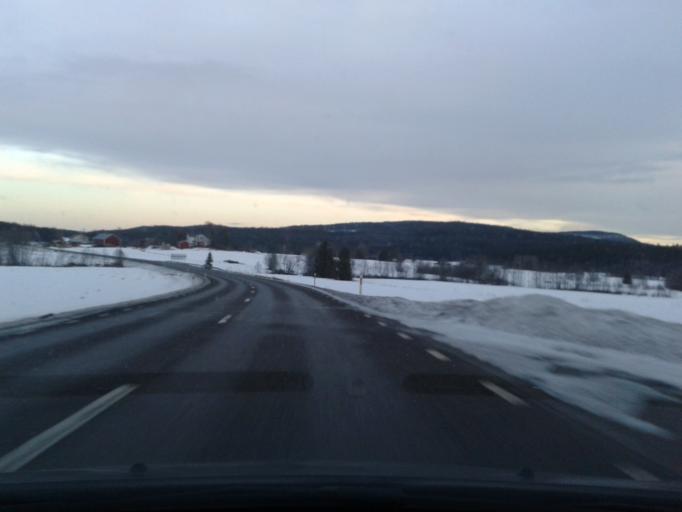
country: SE
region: Vaesternorrland
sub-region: Kramfors Kommun
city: Bollstabruk
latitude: 63.0791
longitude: 17.5408
